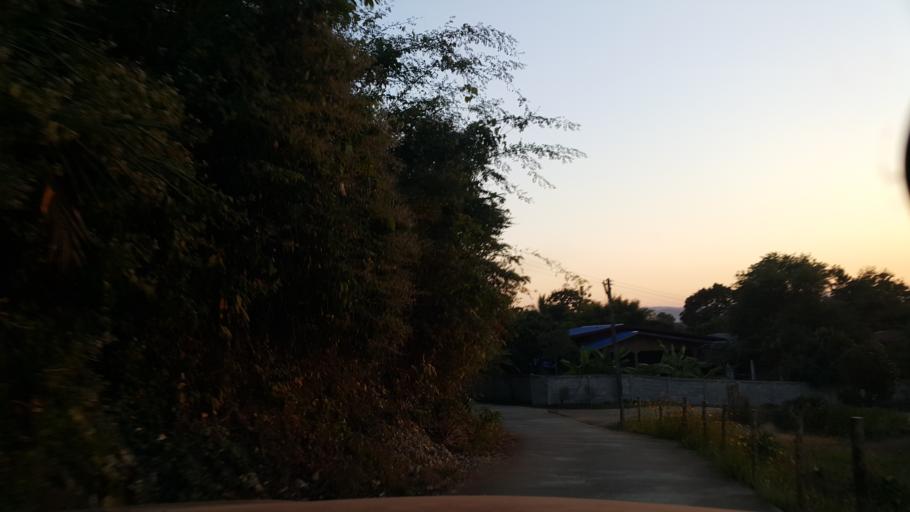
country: TH
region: Phrae
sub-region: Amphoe Wang Chin
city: Wang Chin
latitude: 17.8787
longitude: 99.6235
